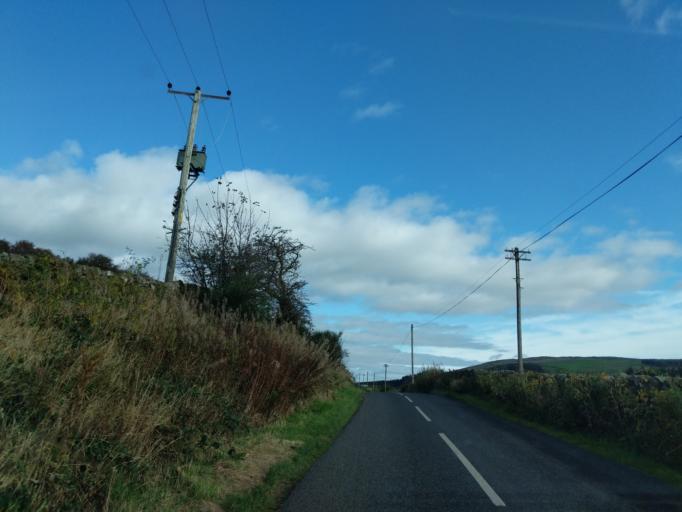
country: GB
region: Scotland
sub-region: Dumfries and Galloway
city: Sanquhar
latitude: 55.1635
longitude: -3.9736
